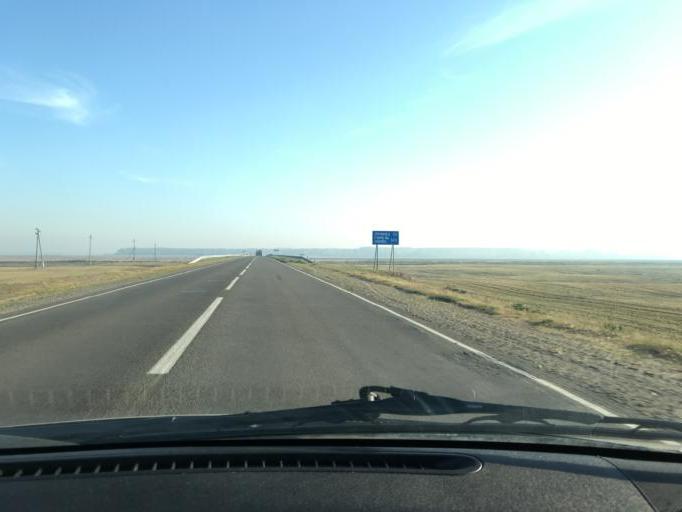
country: BY
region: Brest
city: Asnyezhytsy
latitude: 52.2844
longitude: 26.4084
